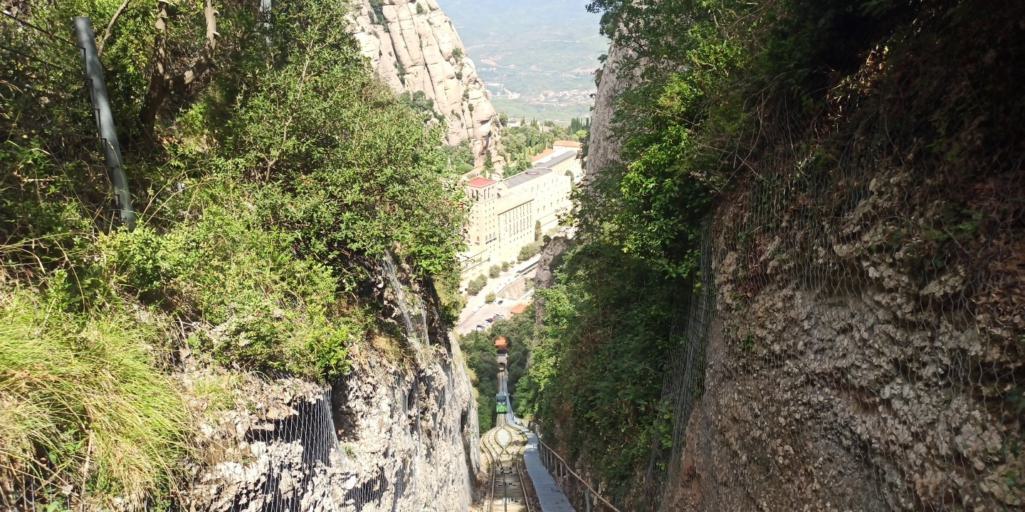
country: ES
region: Catalonia
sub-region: Provincia de Barcelona
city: Collbato
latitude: 41.5898
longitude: 1.8343
